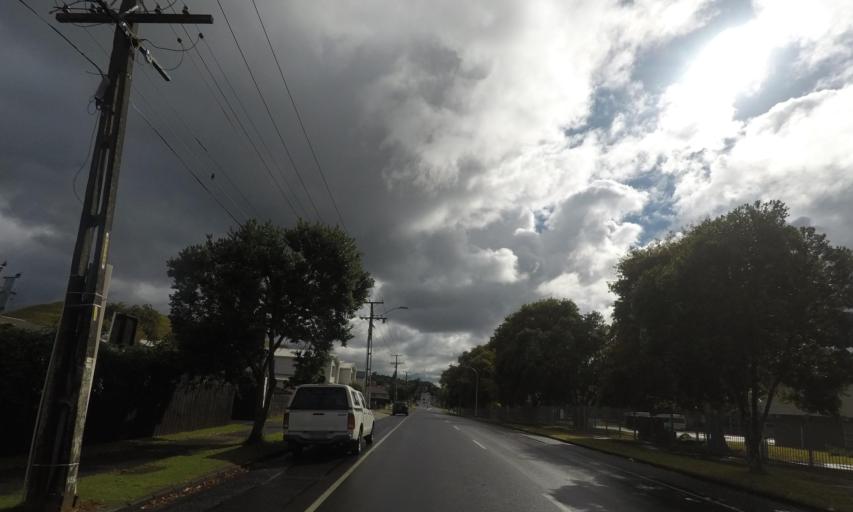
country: NZ
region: Auckland
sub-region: Auckland
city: Mangere
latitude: -36.9569
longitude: 174.7843
